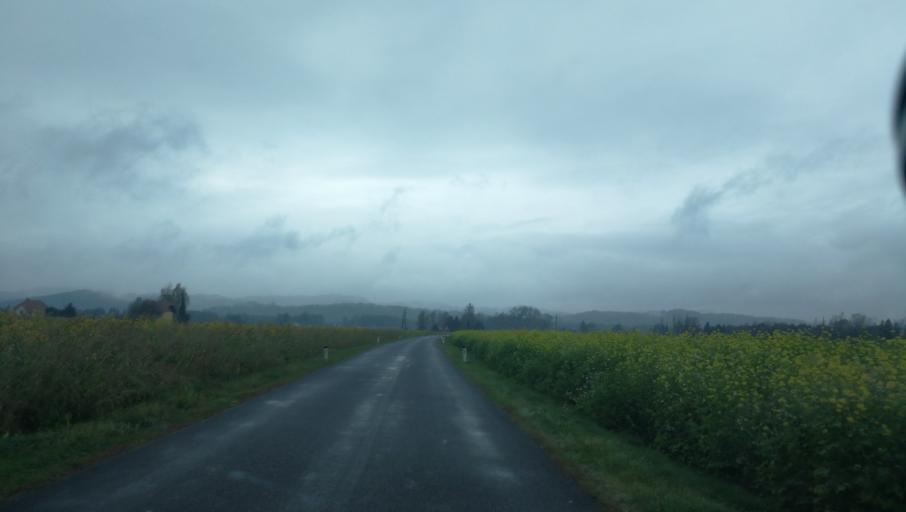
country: AT
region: Styria
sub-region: Politischer Bezirk Leibnitz
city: Sankt Veit am Vogau
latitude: 46.7374
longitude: 15.6216
